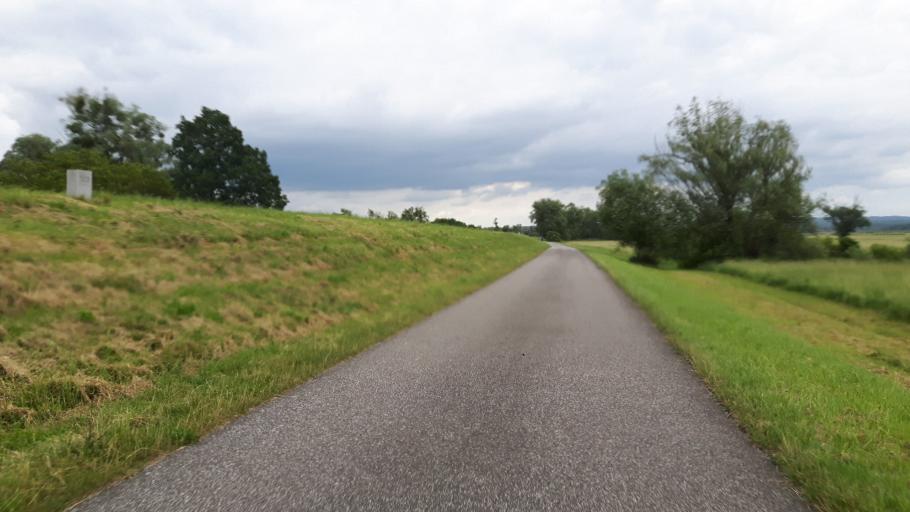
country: DE
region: Brandenburg
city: Schoneberg
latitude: 52.9867
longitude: 14.1546
